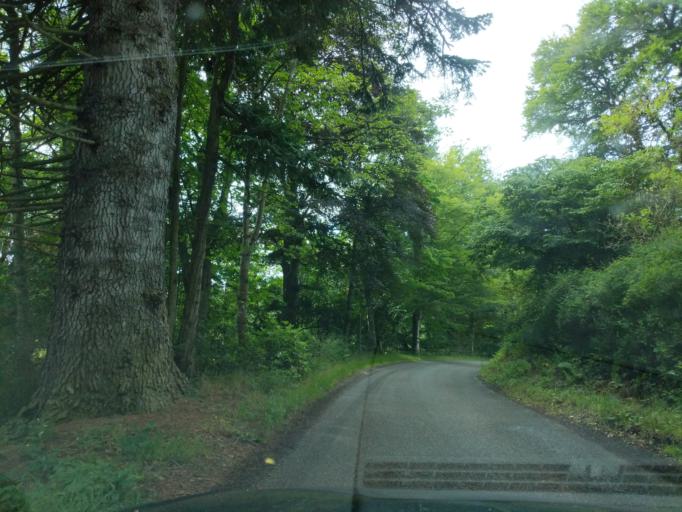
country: GB
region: Scotland
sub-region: Aberdeenshire
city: Aboyne
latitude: 57.0529
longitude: -2.8653
